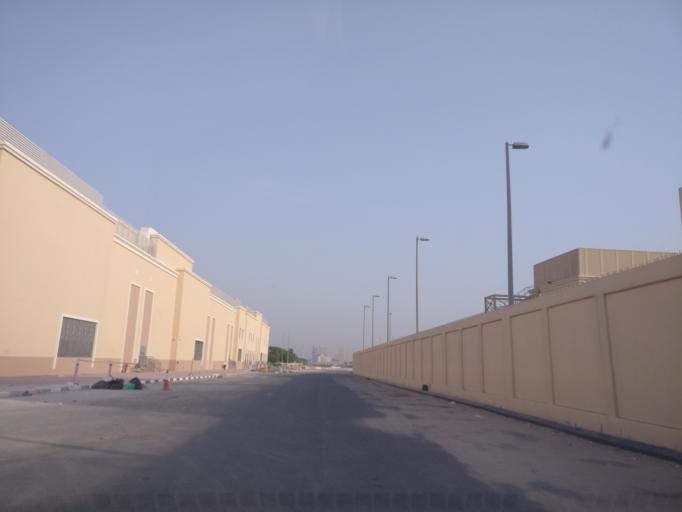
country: AE
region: Dubai
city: Dubai
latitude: 25.0656
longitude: 55.1935
